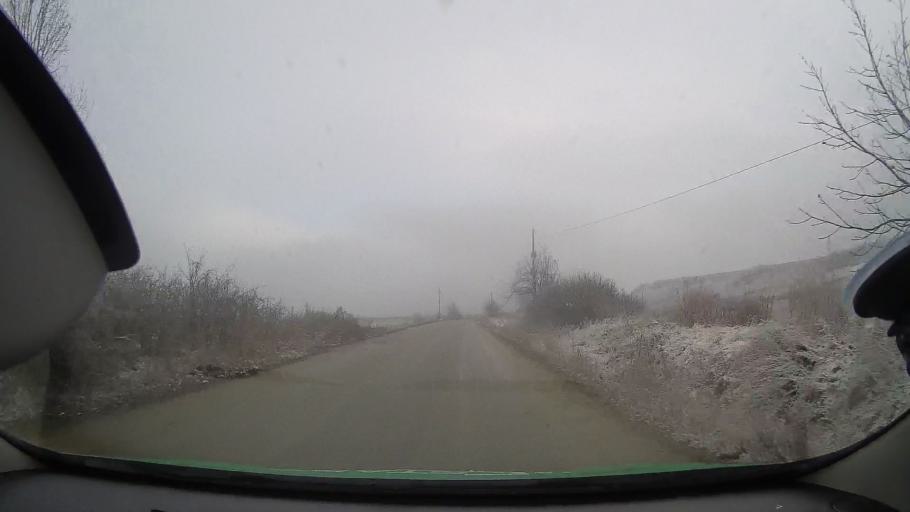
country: RO
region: Alba
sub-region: Oras Ocna Mures
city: Razboieni-Cetate
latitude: 46.3936
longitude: 23.8993
